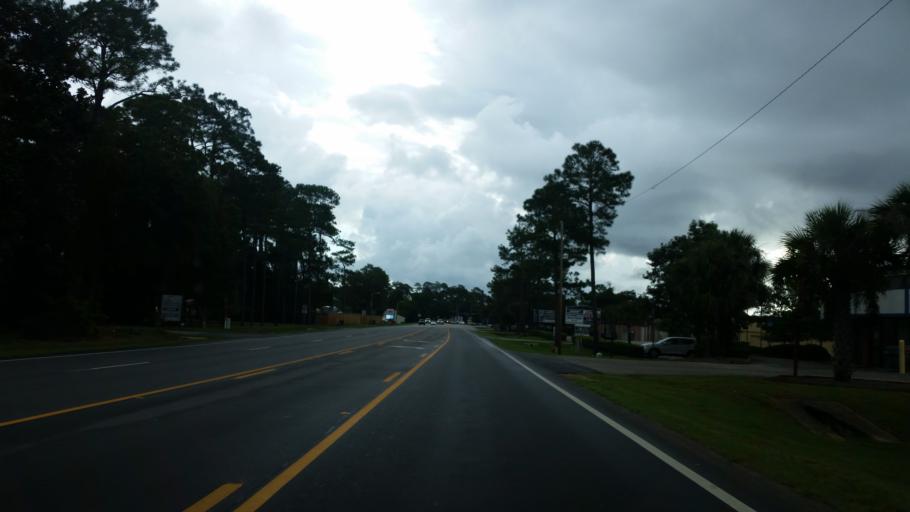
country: US
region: Alabama
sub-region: Baldwin County
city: Orange Beach
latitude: 30.2908
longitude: -87.5855
